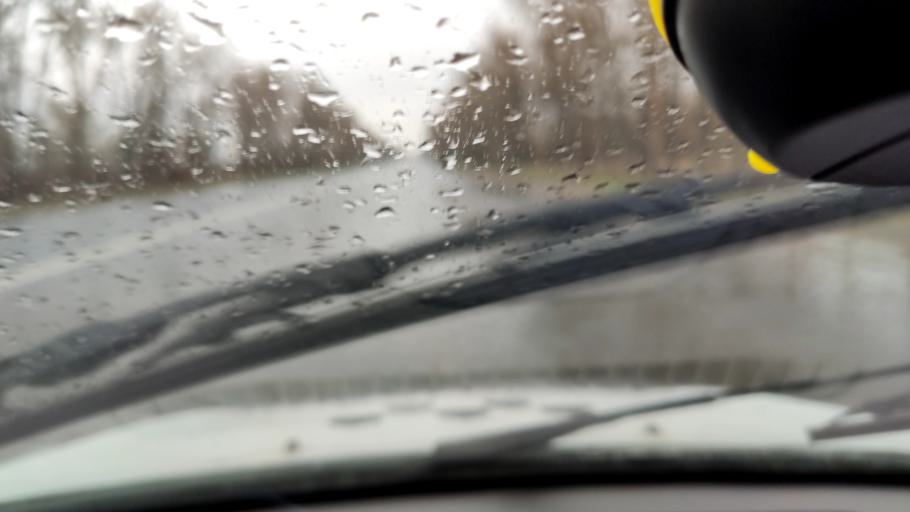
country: RU
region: Samara
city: Podstepki
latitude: 53.5626
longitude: 49.2160
